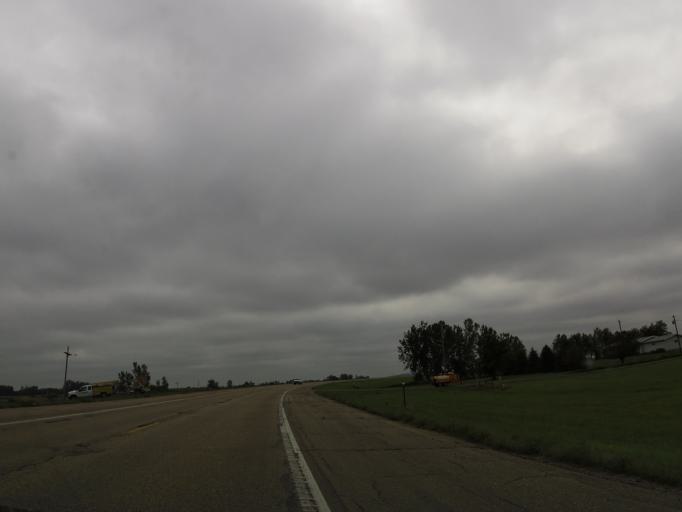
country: US
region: South Dakota
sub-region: Deuel County
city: Clear Lake
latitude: 44.8989
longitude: -96.6795
